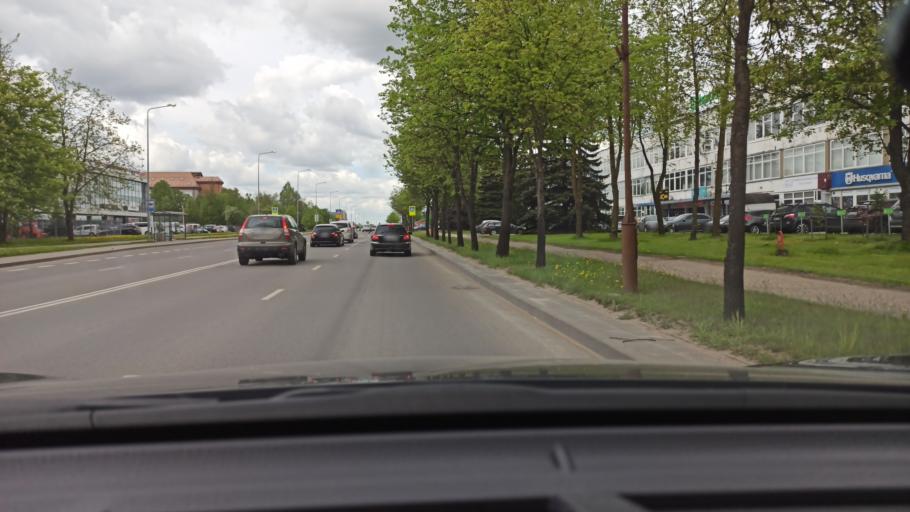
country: LT
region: Siauliu apskritis
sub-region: Siauliai
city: Siauliai
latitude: 55.9099
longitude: 23.3169
